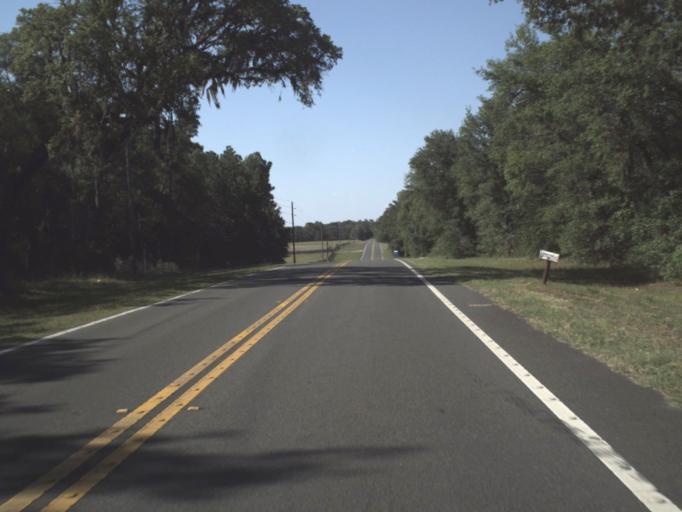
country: US
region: Florida
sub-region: Marion County
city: Dunnellon
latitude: 29.1880
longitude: -82.4386
